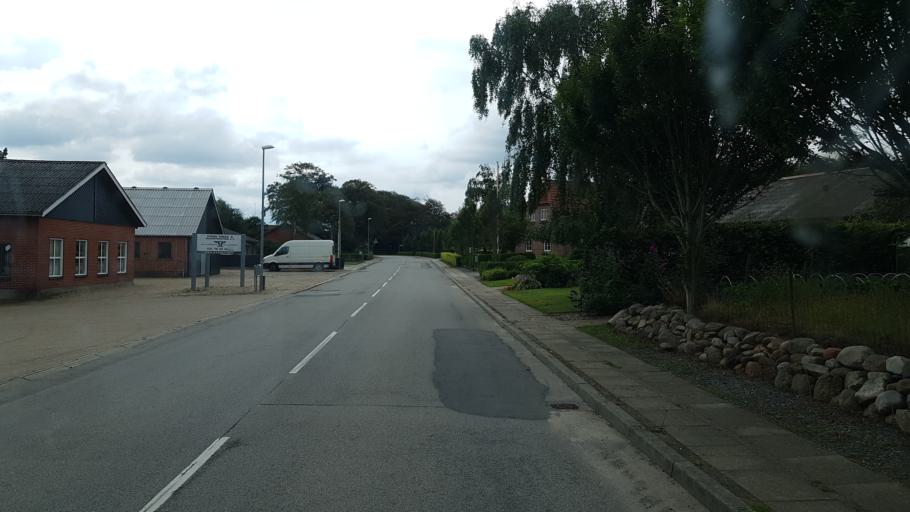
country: DK
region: South Denmark
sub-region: Varde Kommune
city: Varde
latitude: 55.7626
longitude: 8.4331
